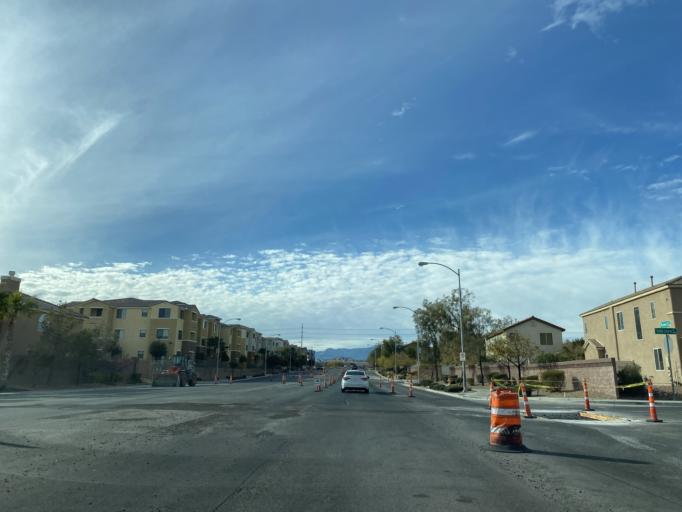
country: US
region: Nevada
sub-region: Clark County
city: Enterprise
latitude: 36.0415
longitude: -115.2382
